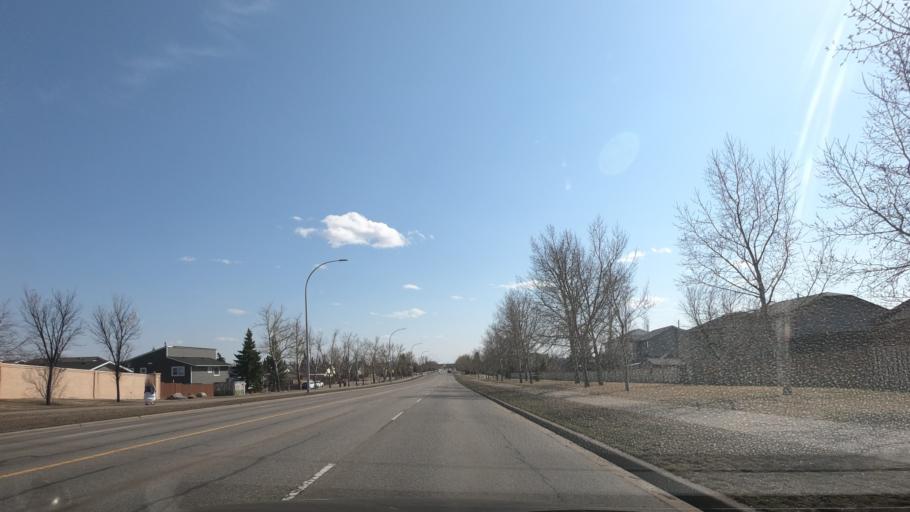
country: CA
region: Alberta
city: Airdrie
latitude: 51.2784
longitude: -113.9899
